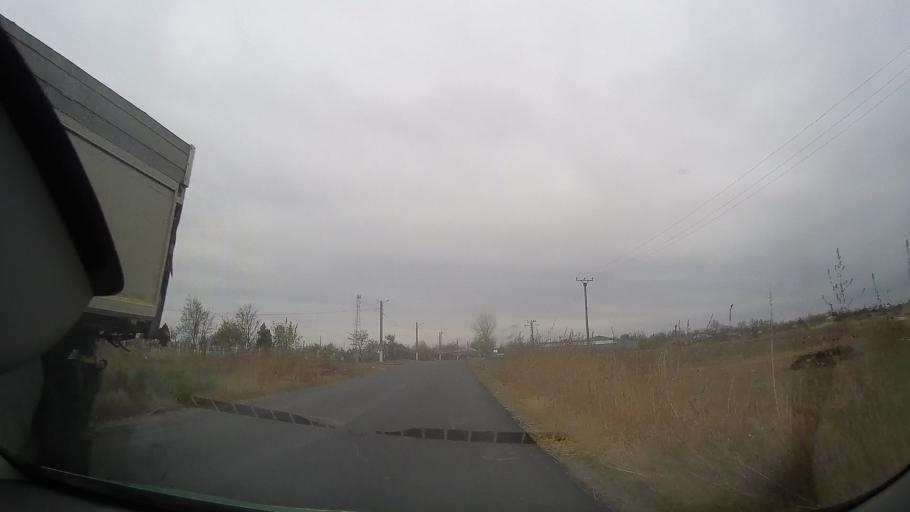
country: RO
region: Braila
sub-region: Comuna Ciresu
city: Ciresu
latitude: 44.9436
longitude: 27.3356
